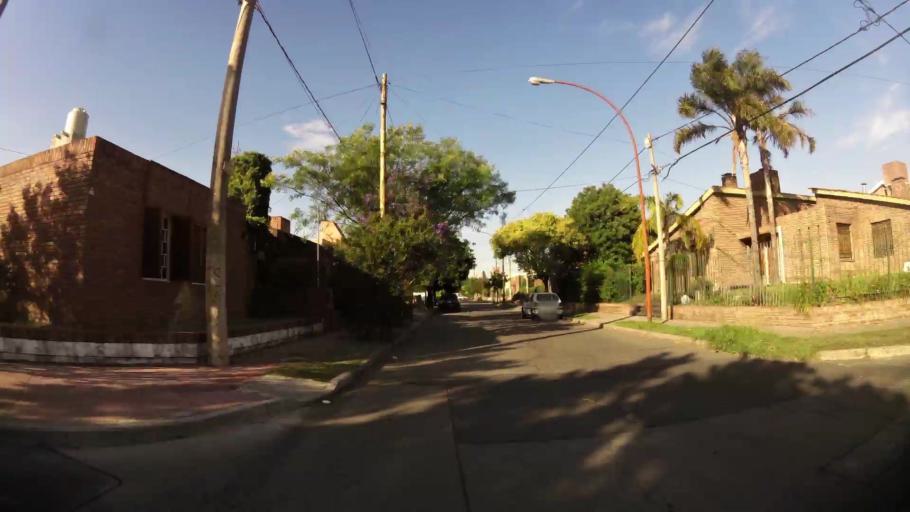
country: AR
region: Cordoba
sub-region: Departamento de Capital
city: Cordoba
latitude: -31.3800
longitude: -64.2363
